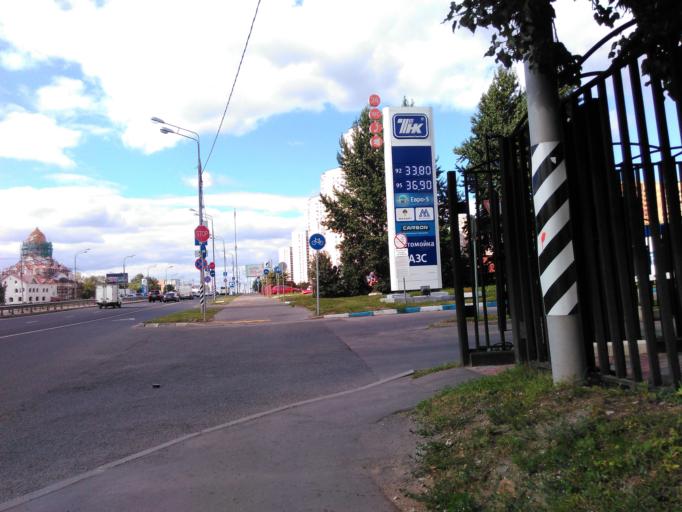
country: RU
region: Moscow
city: Nikol'skoye
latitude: 55.6770
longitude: 37.4842
